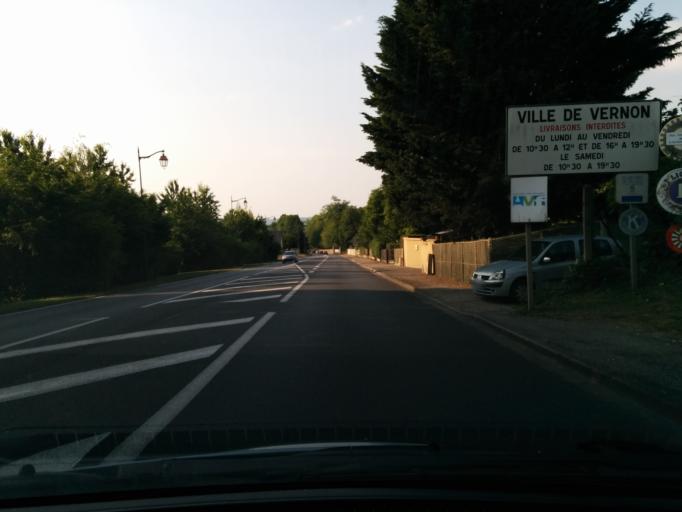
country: FR
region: Haute-Normandie
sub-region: Departement de l'Eure
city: Vernon
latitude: 49.0798
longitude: 1.4643
